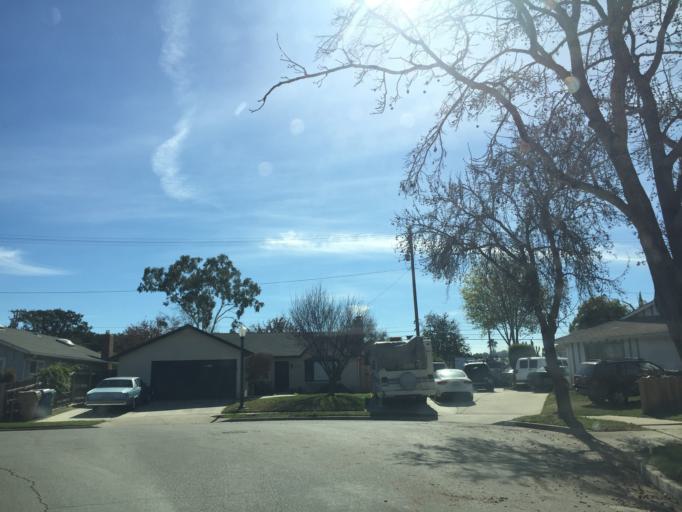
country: US
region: California
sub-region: Santa Barbara County
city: Goleta
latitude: 34.4382
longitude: -119.7846
